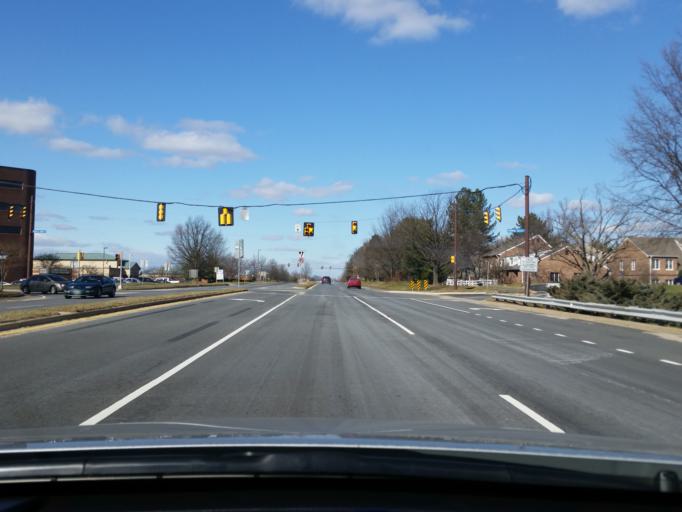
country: US
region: Virginia
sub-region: Fairfax County
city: Reston
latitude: 38.9617
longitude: -77.3542
